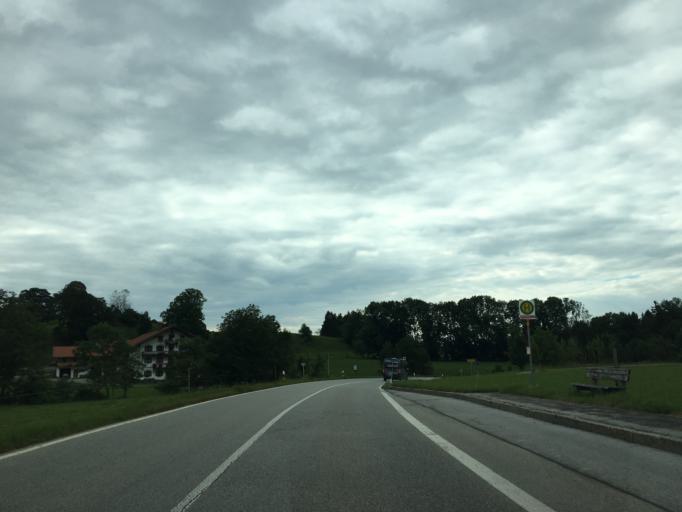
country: DE
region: Bavaria
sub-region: Upper Bavaria
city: Fischbachau
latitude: 47.7608
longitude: 11.9332
